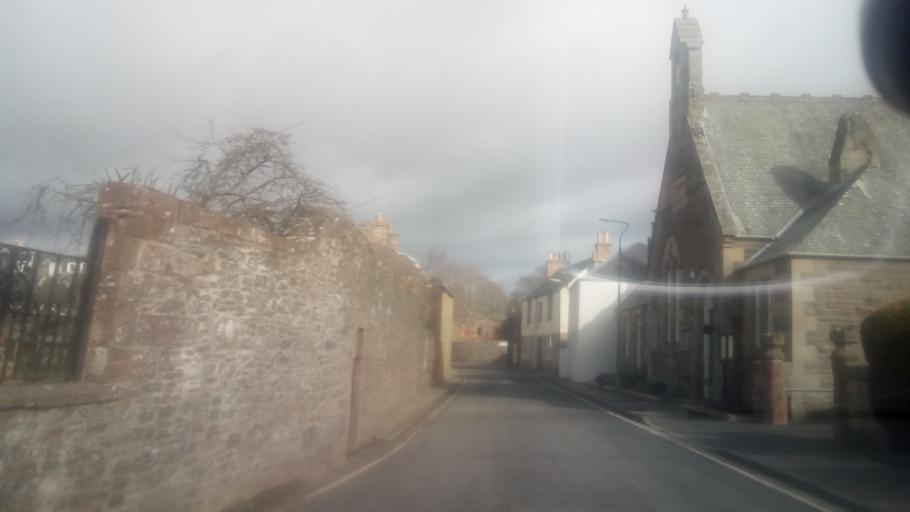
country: GB
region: Scotland
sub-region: The Scottish Borders
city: Melrose
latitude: 55.5996
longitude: -2.7444
